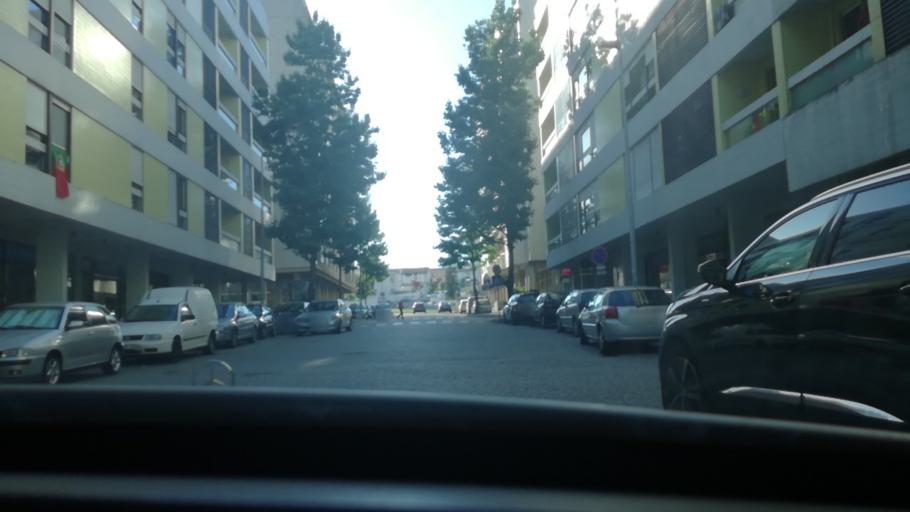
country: PT
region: Porto
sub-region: Maia
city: Maia
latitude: 41.2299
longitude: -8.6121
